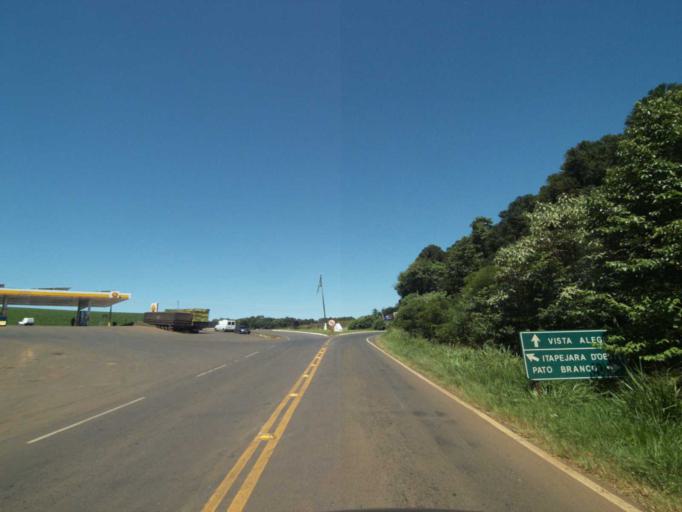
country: BR
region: Parana
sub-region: Coronel Vivida
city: Coronel Vivida
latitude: -25.9786
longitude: -52.8140
